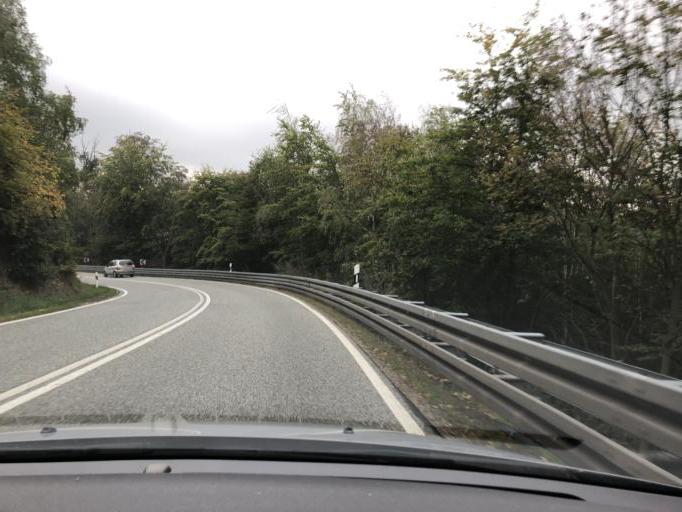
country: DE
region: Saxony-Anhalt
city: Kelbra
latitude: 51.4177
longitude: 11.0631
